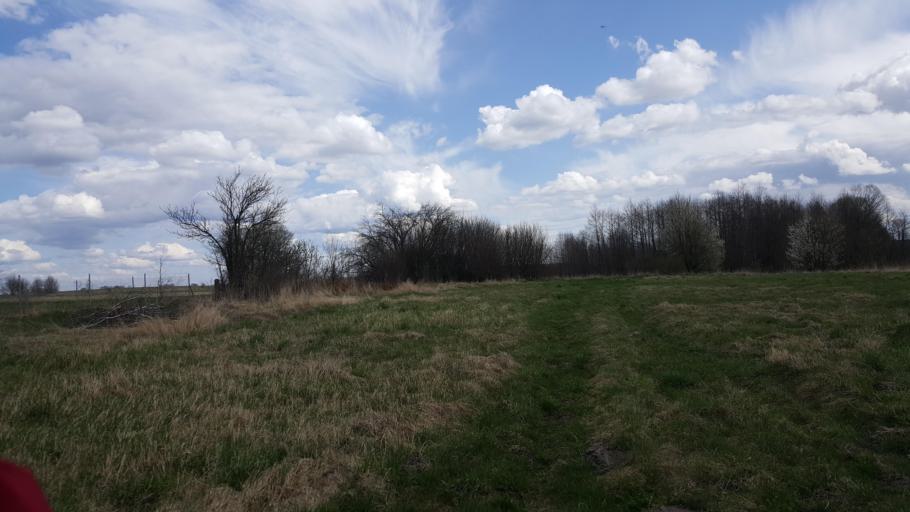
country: BY
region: Brest
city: Kamyanyets
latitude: 52.3493
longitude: 23.7085
